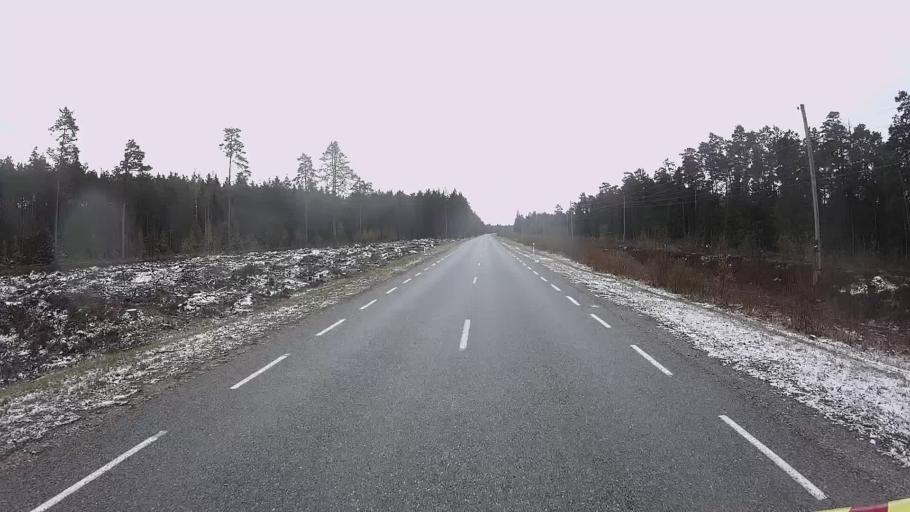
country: EE
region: Hiiumaa
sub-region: Kaerdla linn
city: Kardla
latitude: 59.0233
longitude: 22.6720
